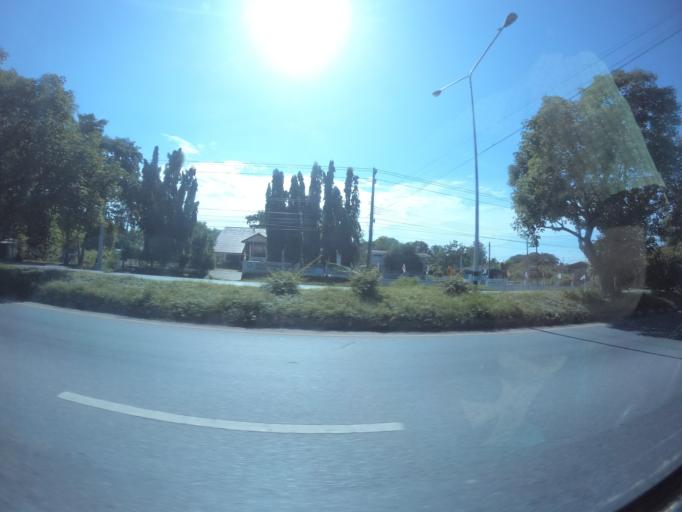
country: TH
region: Nakhon Nayok
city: Ban Na
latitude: 14.2084
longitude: 101.0687
